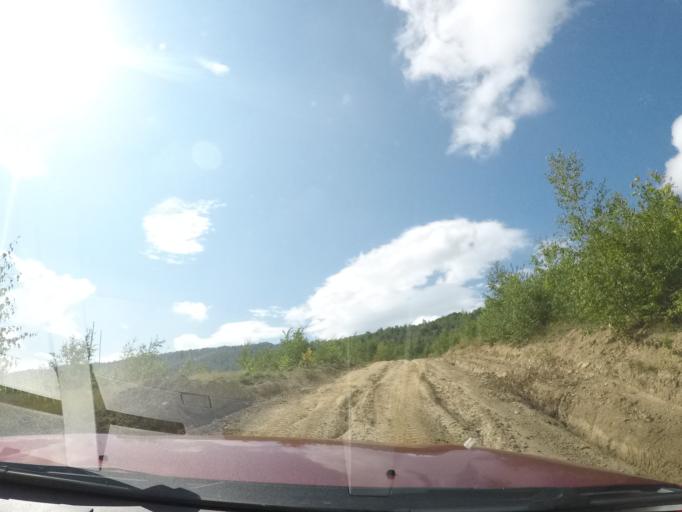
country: UA
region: Zakarpattia
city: Velykyi Bereznyi
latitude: 48.9424
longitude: 22.6695
